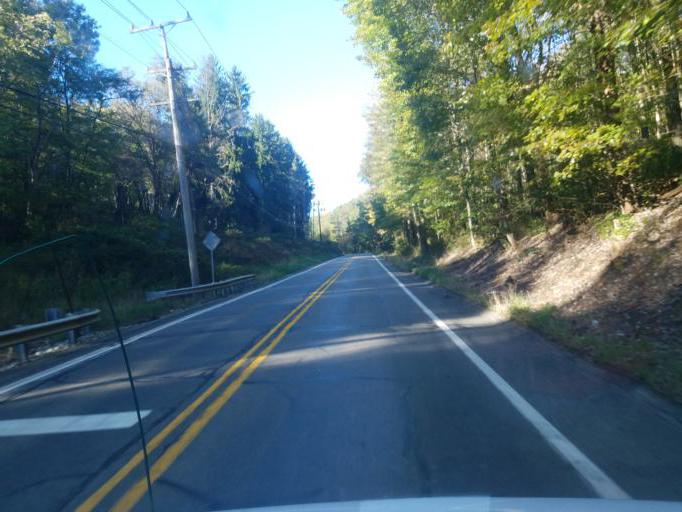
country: US
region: Pennsylvania
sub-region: Beaver County
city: Midland
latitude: 40.5477
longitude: -80.4205
